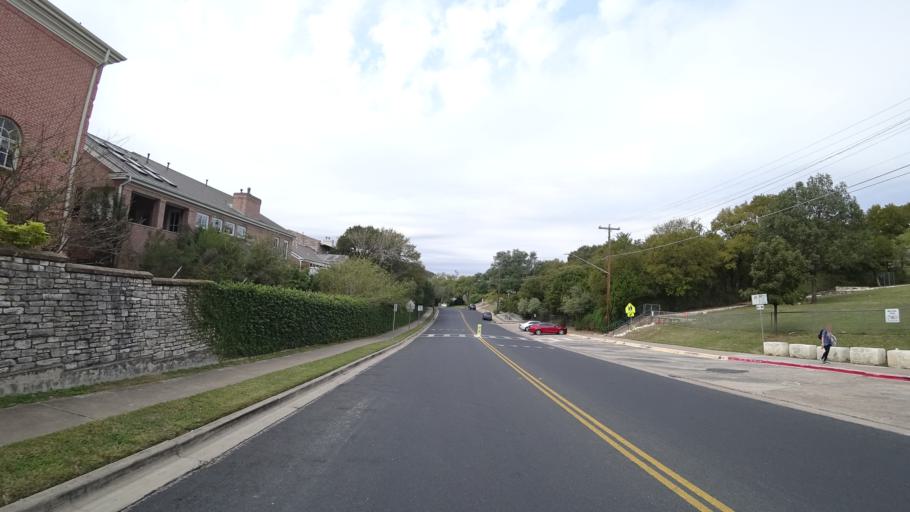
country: US
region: Texas
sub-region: Travis County
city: Rollingwood
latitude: 30.3033
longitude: -97.7656
